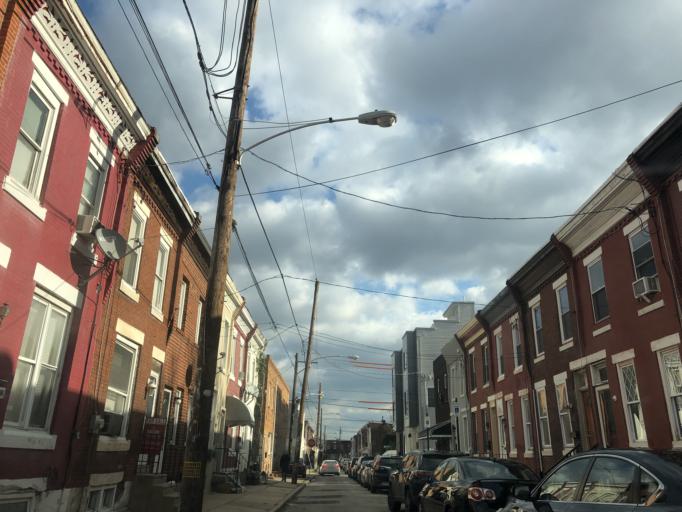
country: US
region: Pennsylvania
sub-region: Philadelphia County
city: Philadelphia
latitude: 39.9298
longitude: -75.1791
